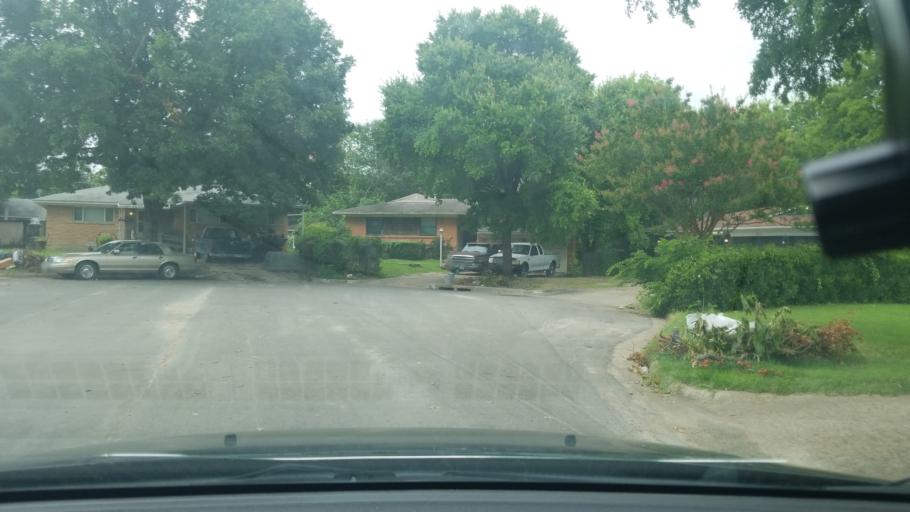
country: US
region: Texas
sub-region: Dallas County
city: Balch Springs
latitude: 32.7704
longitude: -96.6920
